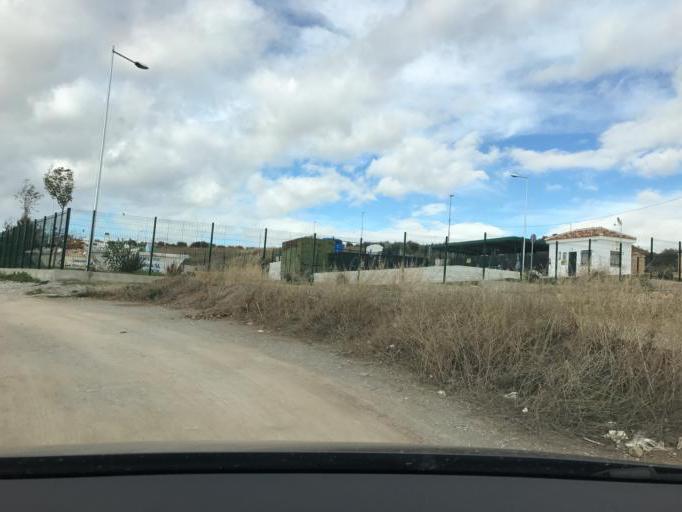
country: ES
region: Andalusia
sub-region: Provincia de Granada
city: Peligros
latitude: 37.2357
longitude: -3.6328
